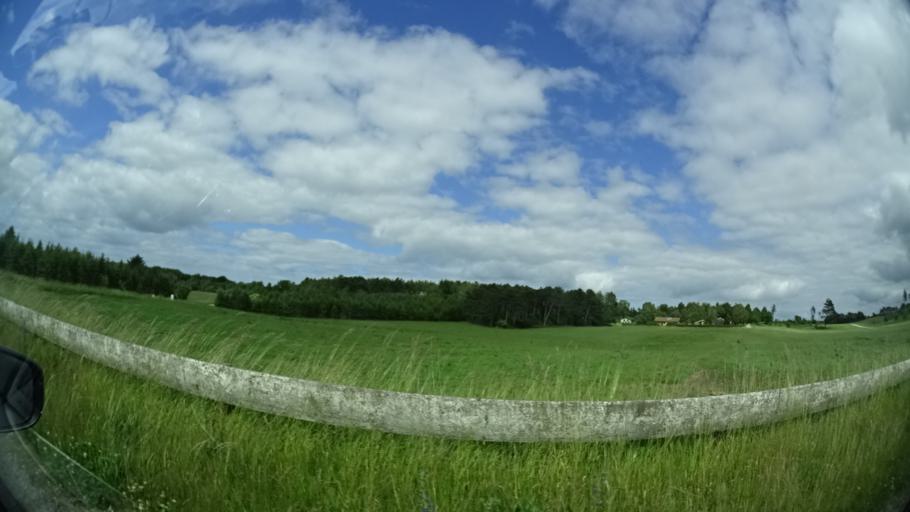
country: DK
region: Central Jutland
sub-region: Norddjurs Kommune
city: Grenaa
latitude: 56.5229
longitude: 10.7159
